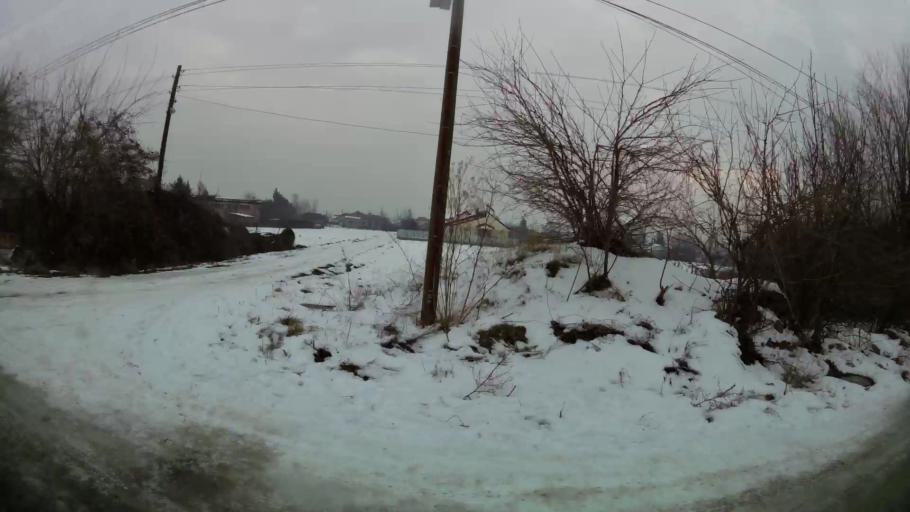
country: MK
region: Saraj
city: Saraj
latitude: 42.0434
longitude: 21.3532
